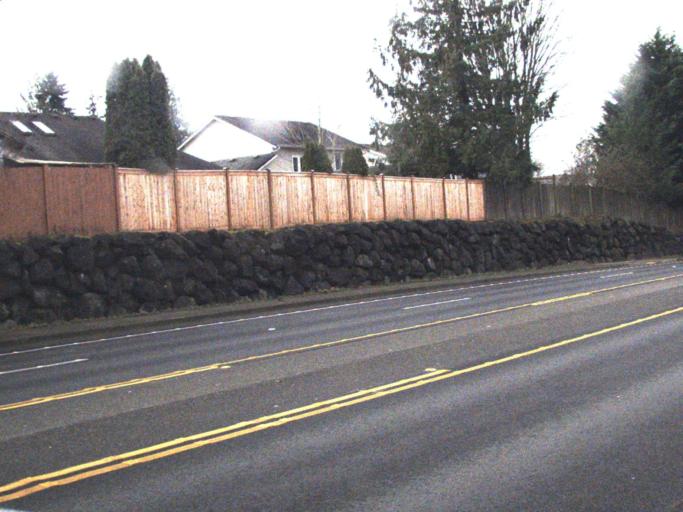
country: US
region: Washington
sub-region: Snohomish County
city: Marysville
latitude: 48.0537
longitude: -122.1326
